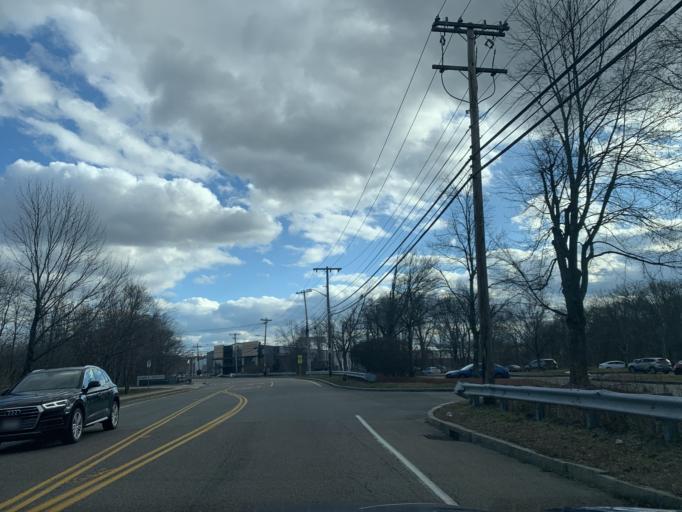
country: US
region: Massachusetts
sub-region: Norfolk County
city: Norwood
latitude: 42.2013
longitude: -71.1757
